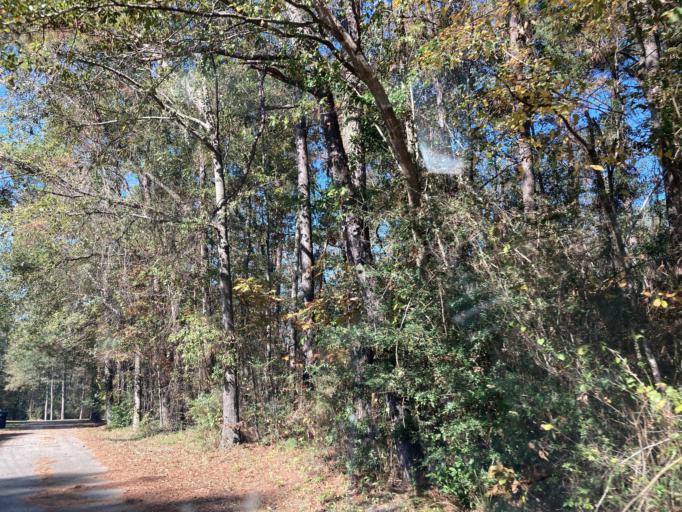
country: US
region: Mississippi
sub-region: Lamar County
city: Sumrall
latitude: 31.3514
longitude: -89.4752
